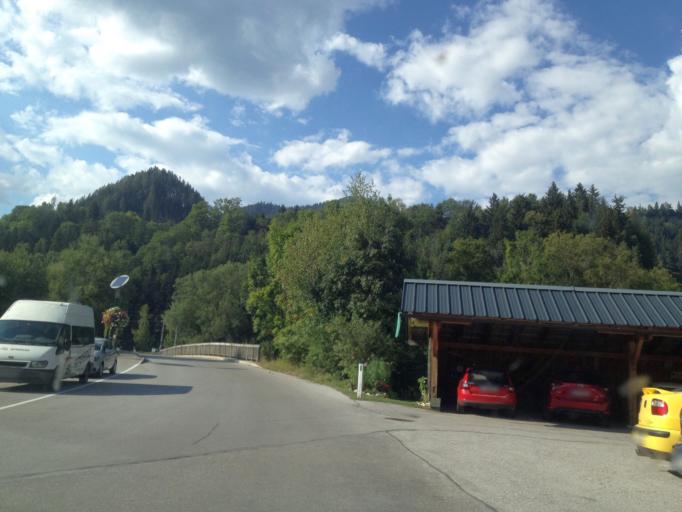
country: AT
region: Styria
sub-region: Politischer Bezirk Liezen
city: Schladming
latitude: 47.3877
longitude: 13.6174
